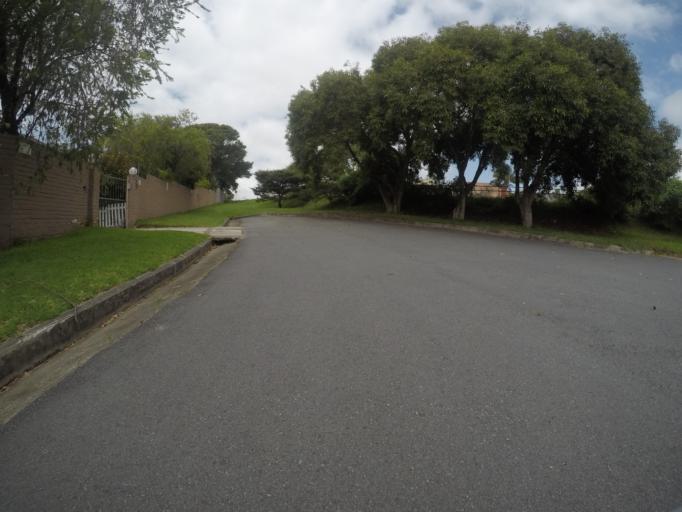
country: ZA
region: Eastern Cape
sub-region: Buffalo City Metropolitan Municipality
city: East London
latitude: -32.9899
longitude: 27.9208
